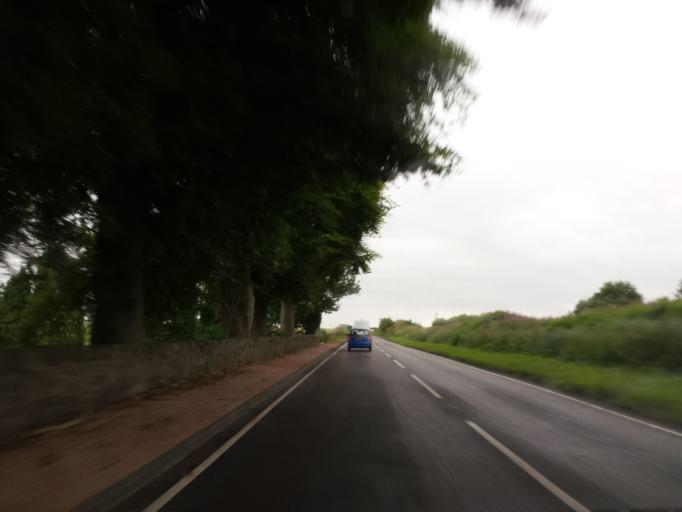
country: GB
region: Scotland
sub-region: Fife
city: Leuchars
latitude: 56.3893
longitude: -2.8995
